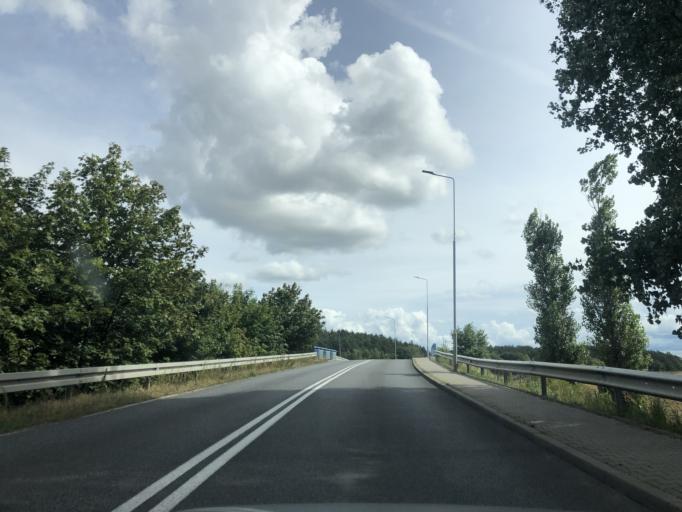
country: PL
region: Greater Poland Voivodeship
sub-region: Powiat czarnkowsko-trzcianecki
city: Trzcianka
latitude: 53.0432
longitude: 16.4776
